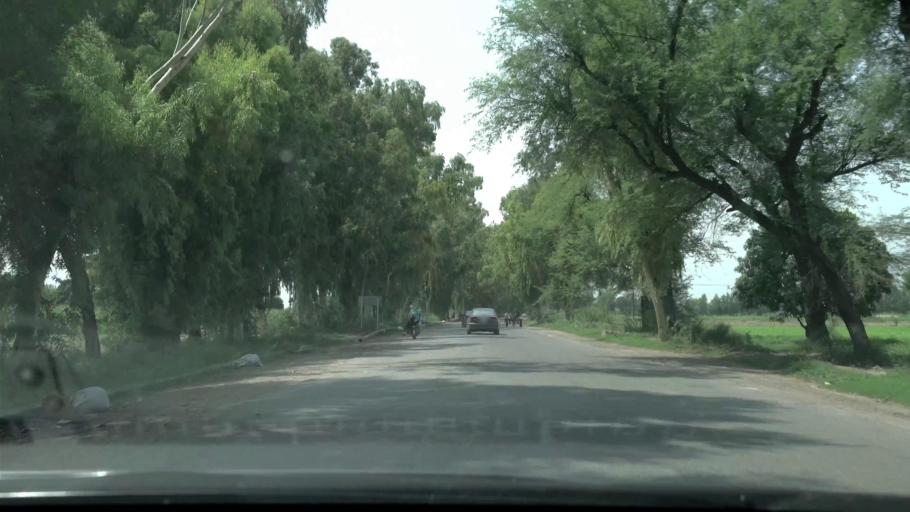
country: PK
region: Punjab
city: Gojra
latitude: 31.1702
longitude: 72.6211
